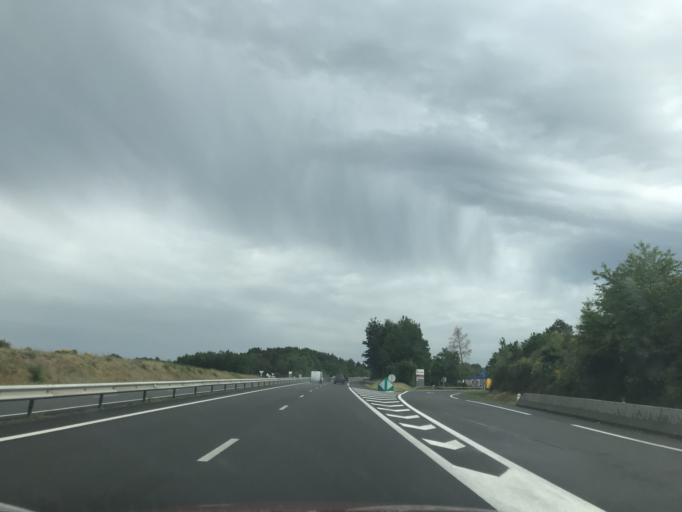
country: FR
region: Auvergne
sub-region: Departement de l'Allier
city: Bellenaves
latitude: 46.2338
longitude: 3.0984
